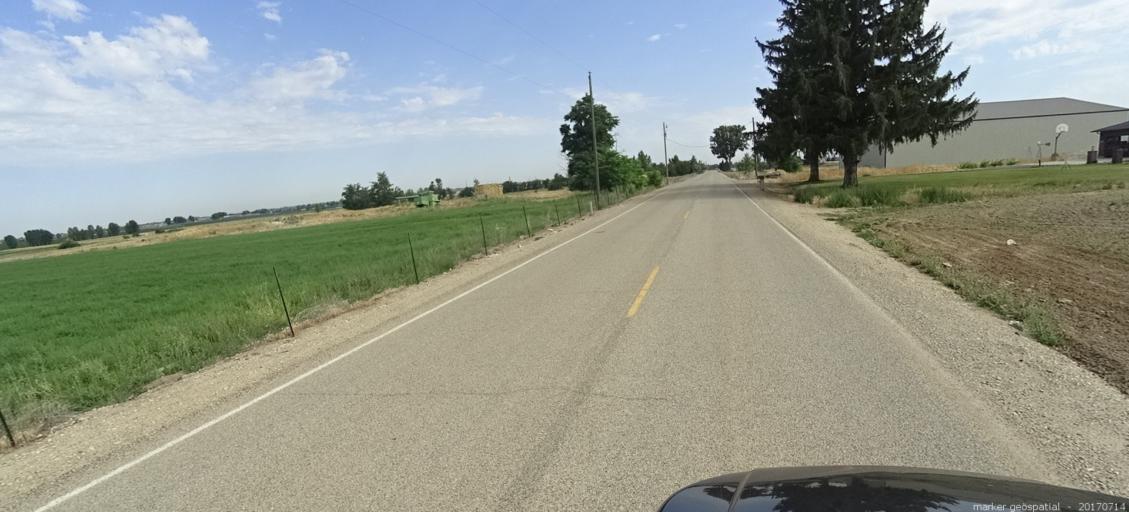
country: US
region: Idaho
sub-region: Ada County
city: Kuna
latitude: 43.4925
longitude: -116.3543
